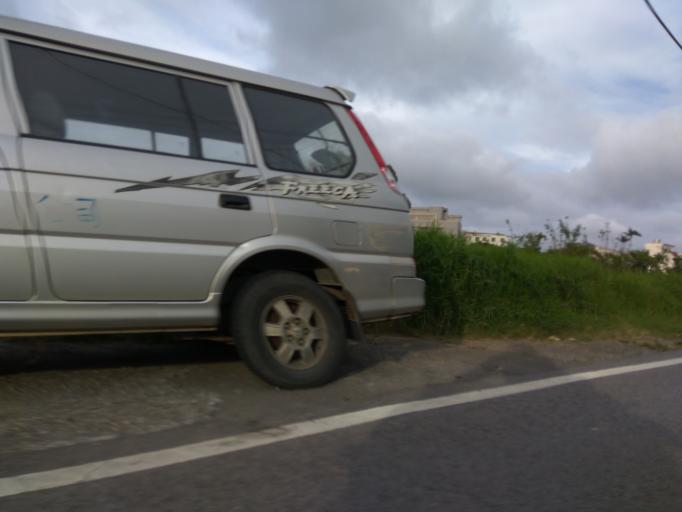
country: TW
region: Taiwan
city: Daxi
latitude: 24.9212
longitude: 121.2018
